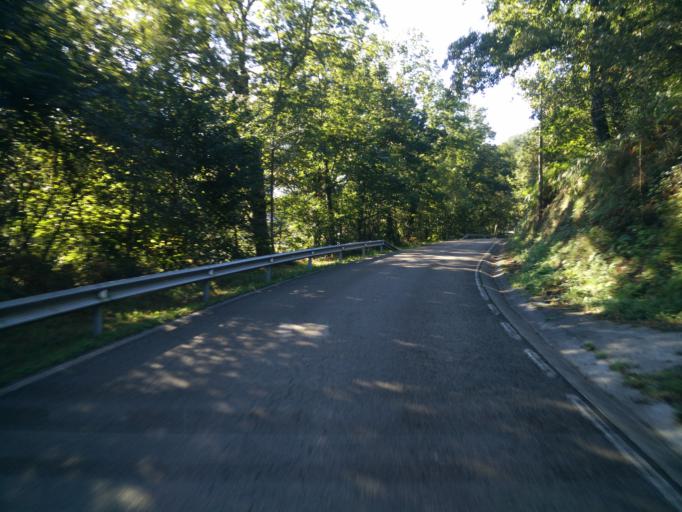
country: ES
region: Cantabria
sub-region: Provincia de Cantabria
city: San Pedro del Romeral
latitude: 43.1453
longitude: -3.8185
